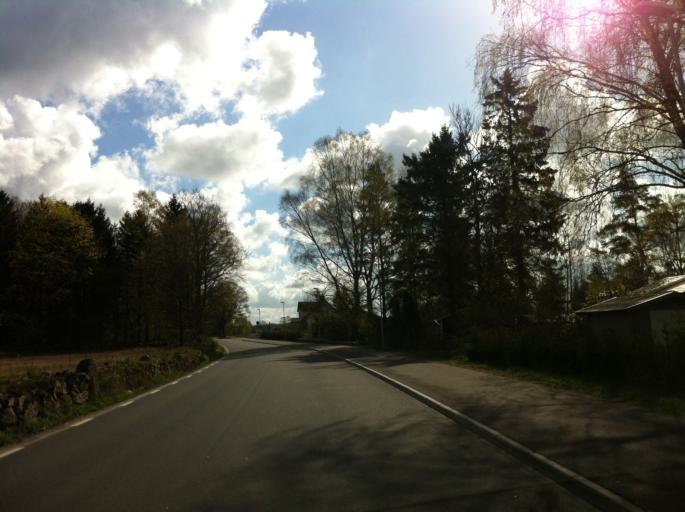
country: SE
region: Skane
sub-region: Hoors Kommun
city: Satofta
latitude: 55.9082
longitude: 13.5640
